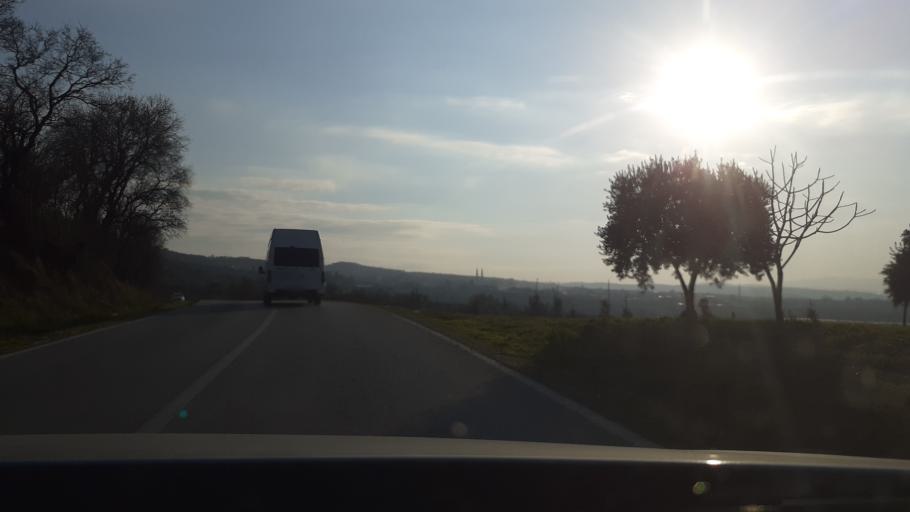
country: TR
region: Hatay
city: Oymakli
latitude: 36.1205
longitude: 36.3055
